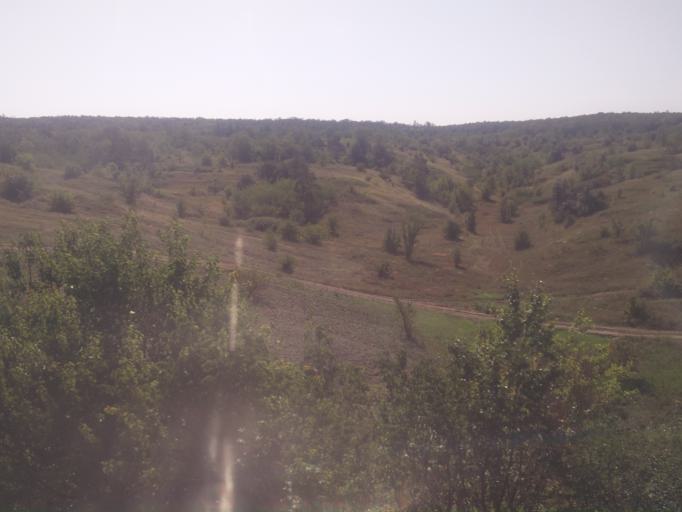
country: RU
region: Rostov
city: Krasnyy Sulin
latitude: 47.8777
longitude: 40.1300
